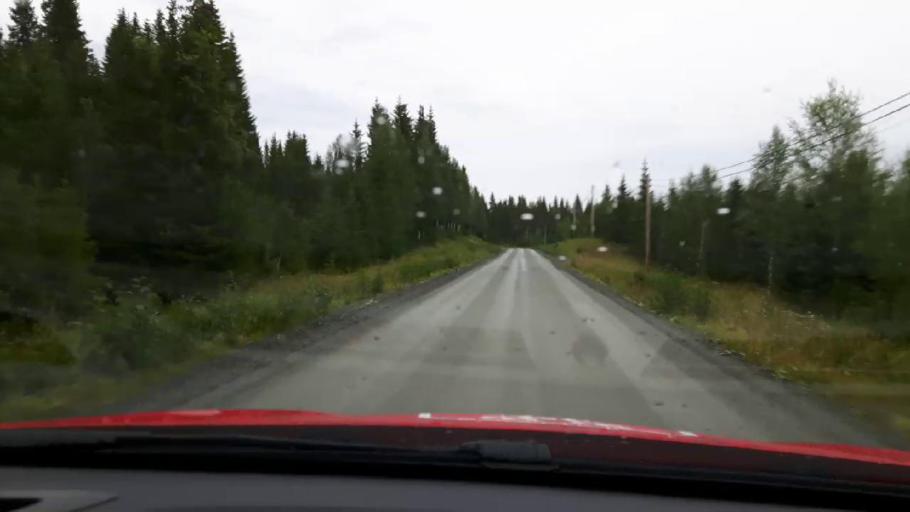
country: SE
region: Jaemtland
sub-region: Are Kommun
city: Are
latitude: 63.4815
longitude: 12.7957
